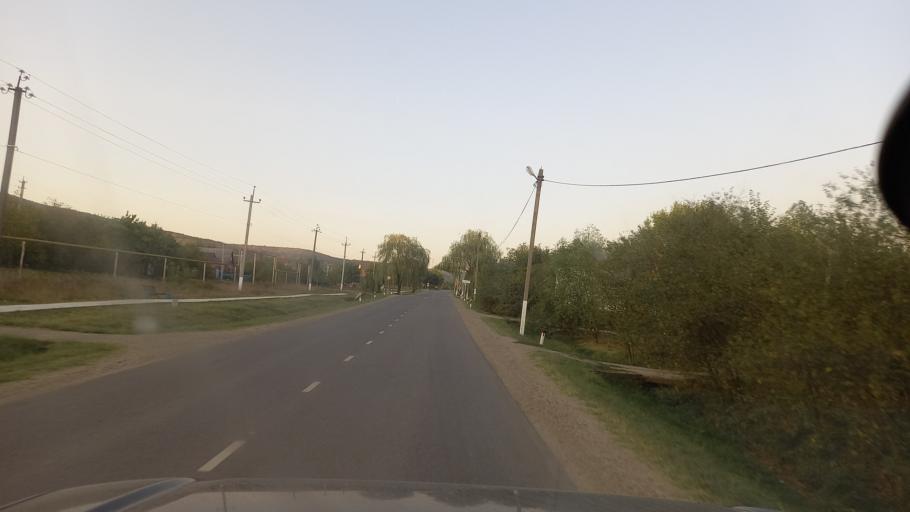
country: RU
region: Krasnodarskiy
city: Smolenskaya
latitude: 44.7735
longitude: 38.7854
